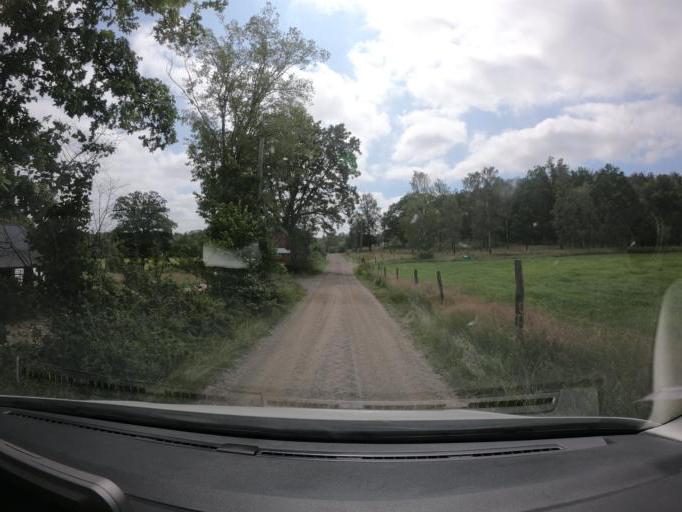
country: SE
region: Skane
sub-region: Hassleholms Kommun
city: Sosdala
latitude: 56.0526
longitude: 13.5713
